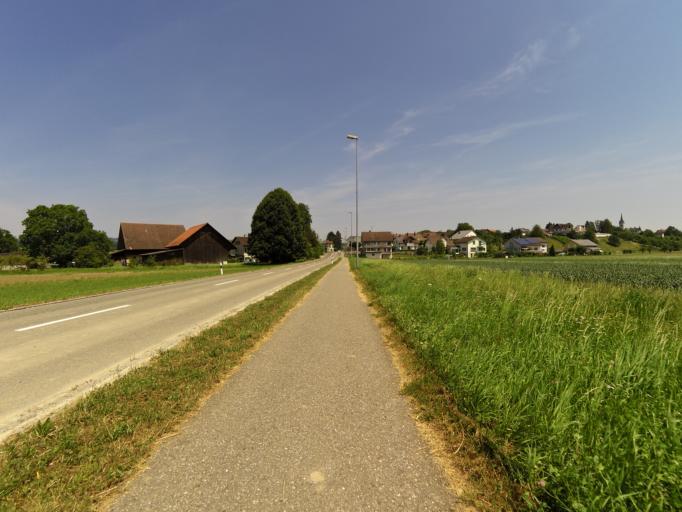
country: CH
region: Thurgau
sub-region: Weinfelden District
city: Wigoltingen
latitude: 47.5948
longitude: 9.0234
